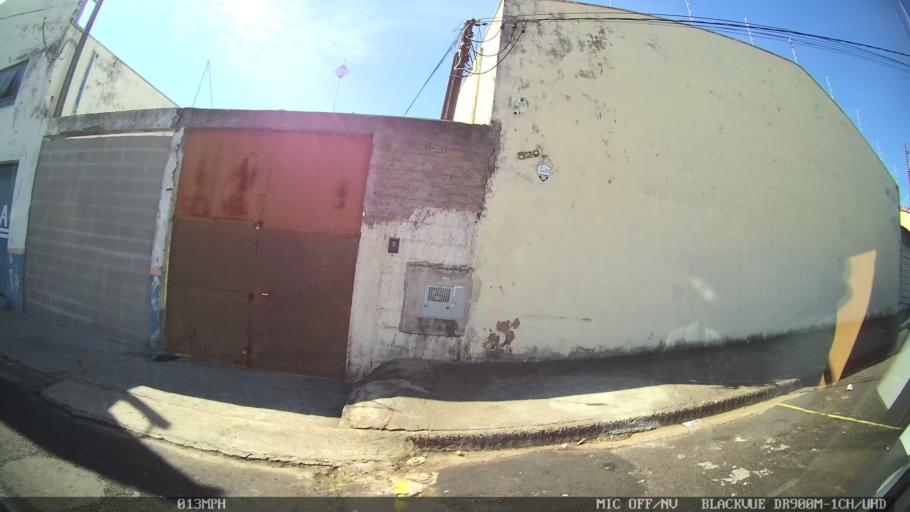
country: BR
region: Sao Paulo
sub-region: Franca
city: Franca
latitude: -20.5556
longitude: -47.4000
